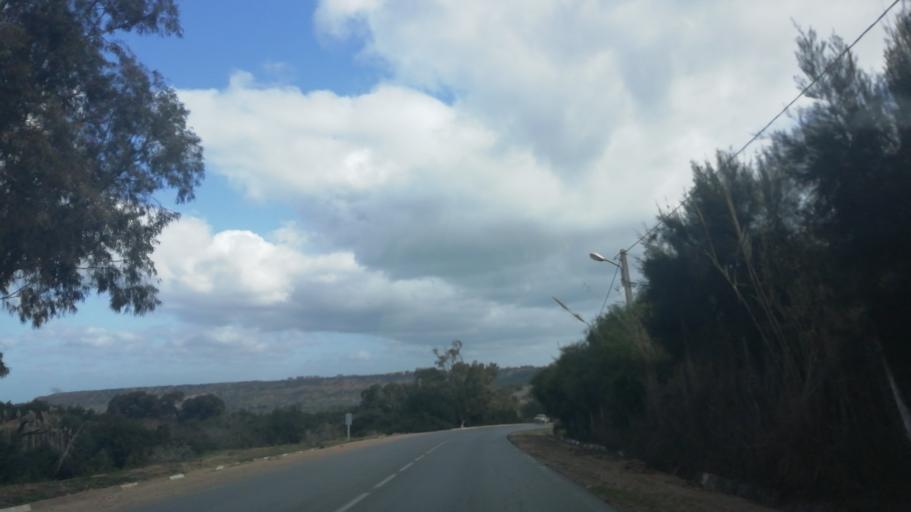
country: DZ
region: Relizane
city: Mazouna
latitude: 36.2941
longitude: 0.6561
